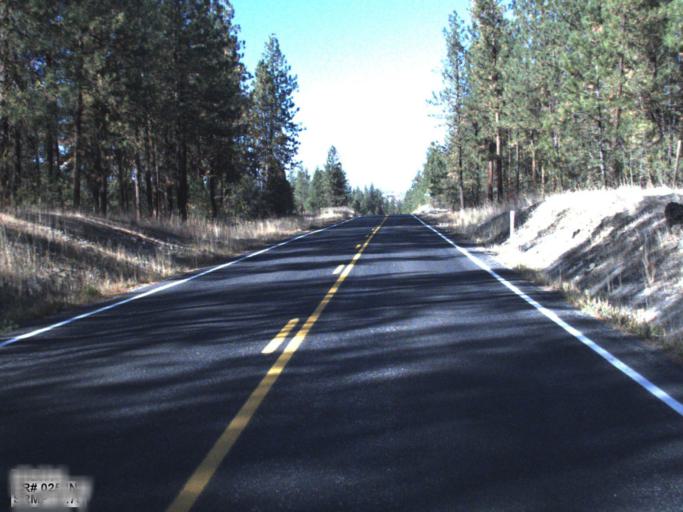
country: US
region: Washington
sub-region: Lincoln County
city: Davenport
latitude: 48.0806
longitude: -118.2004
